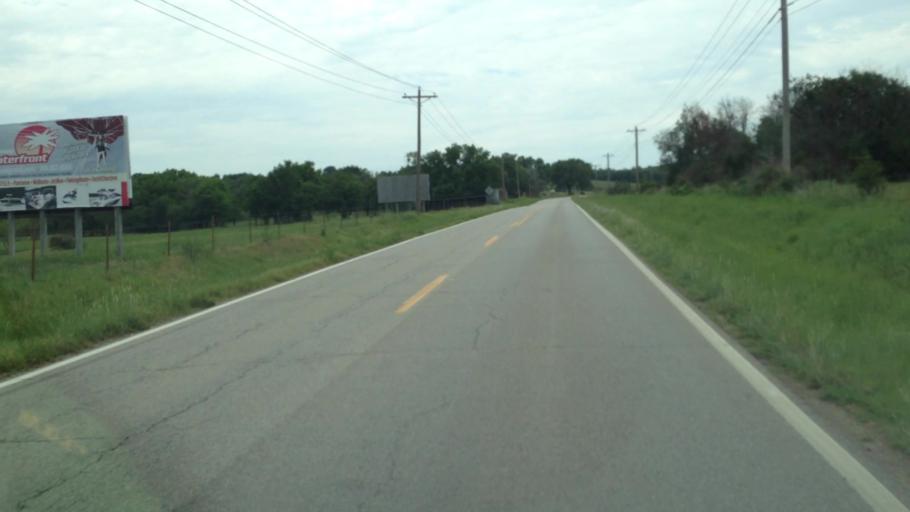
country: US
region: Oklahoma
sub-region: Delaware County
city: Cleora
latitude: 36.5795
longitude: -94.9707
